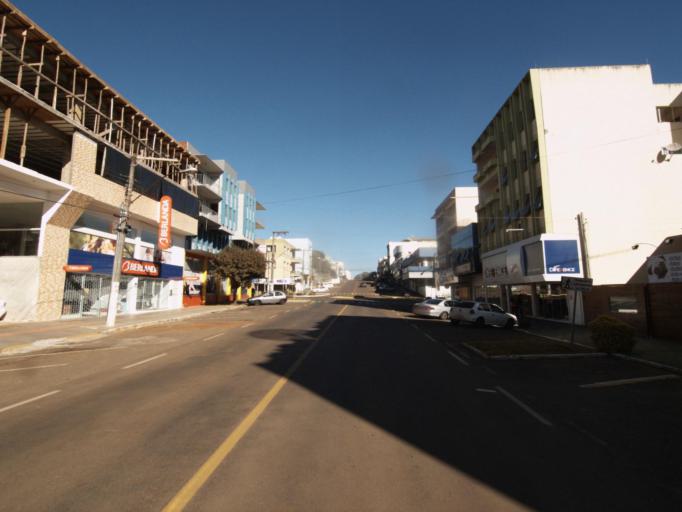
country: AR
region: Misiones
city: Bernardo de Irigoyen
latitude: -26.7276
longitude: -53.5203
